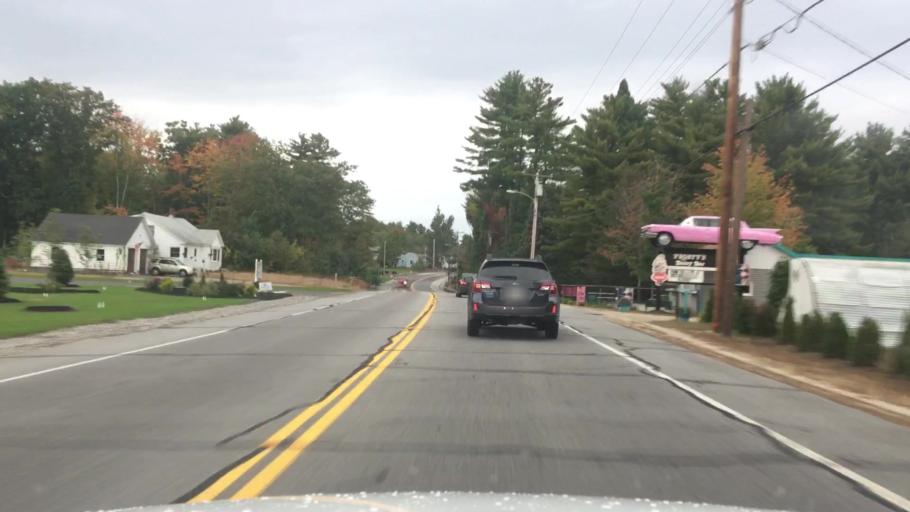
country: US
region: Maine
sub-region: York County
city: Waterboro
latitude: 43.5289
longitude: -70.7191
